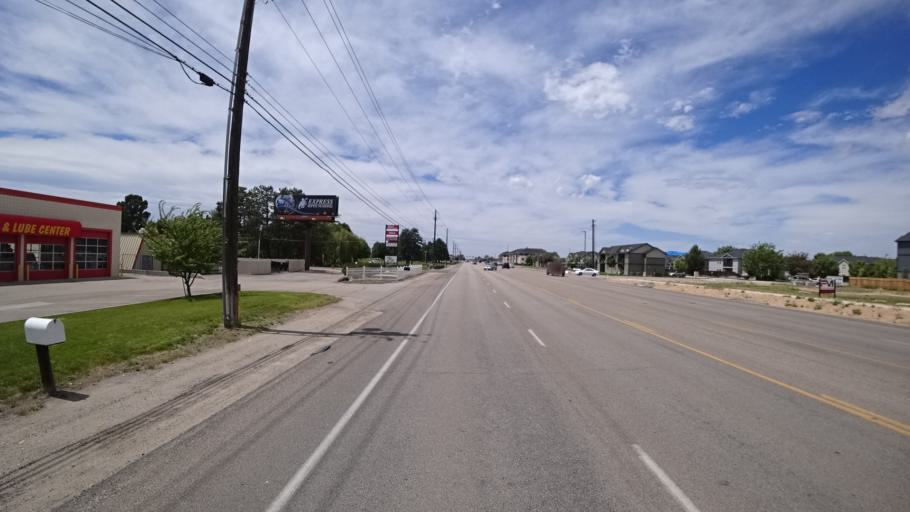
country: US
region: Idaho
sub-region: Ada County
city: Meridian
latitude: 43.6194
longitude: -116.3286
